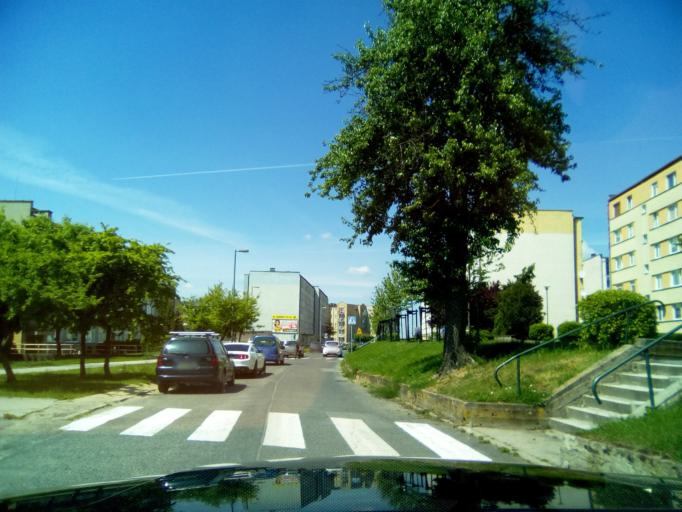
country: PL
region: Greater Poland Voivodeship
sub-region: Powiat gnieznienski
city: Gniezno
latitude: 52.5495
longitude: 17.5997
